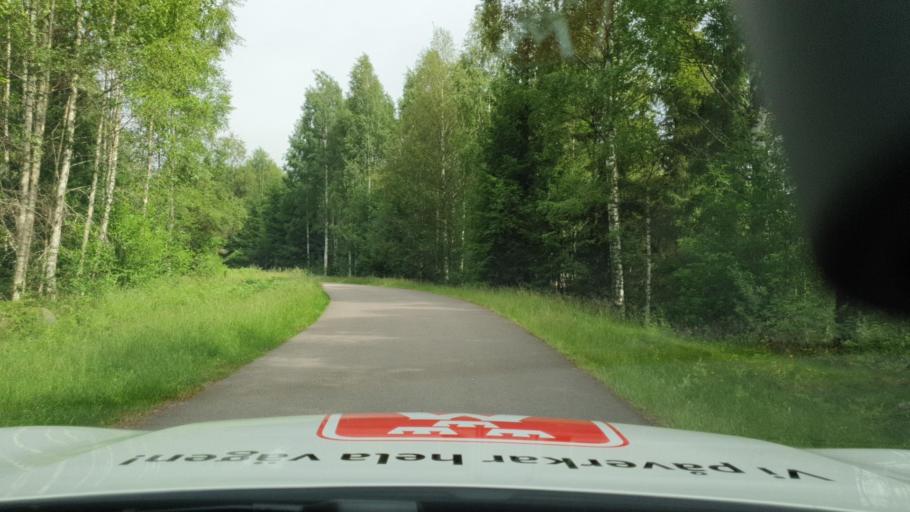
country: SE
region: Vaermland
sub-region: Sunne Kommun
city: Sunne
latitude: 59.9713
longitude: 13.1005
